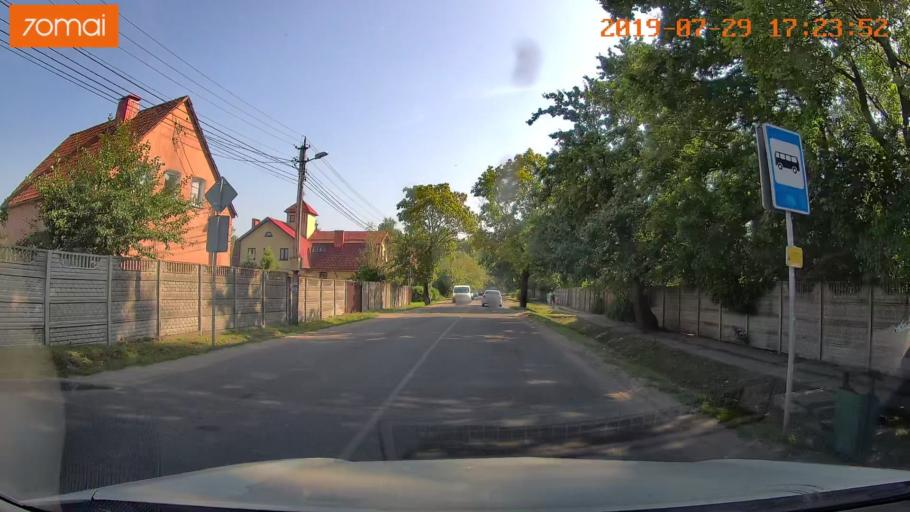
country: RU
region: Kaliningrad
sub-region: Gorod Kaliningrad
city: Kaliningrad
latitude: 54.7637
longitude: 20.4437
